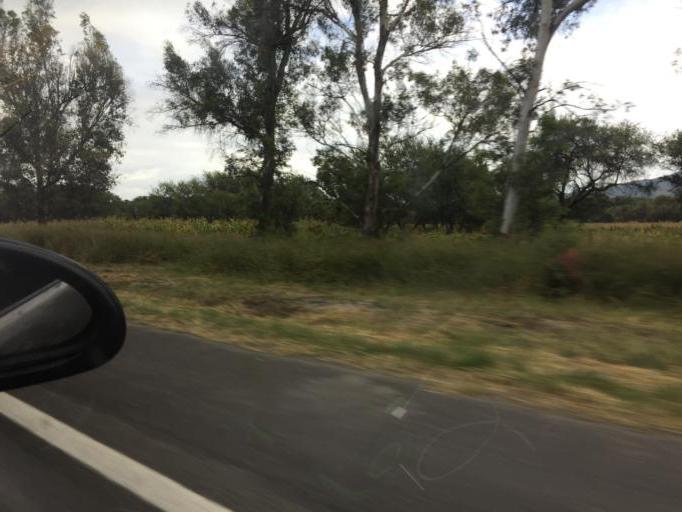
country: MX
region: Jalisco
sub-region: Ocotlan
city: Joconoxtle (La Tuna)
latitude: 20.3795
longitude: -102.6900
